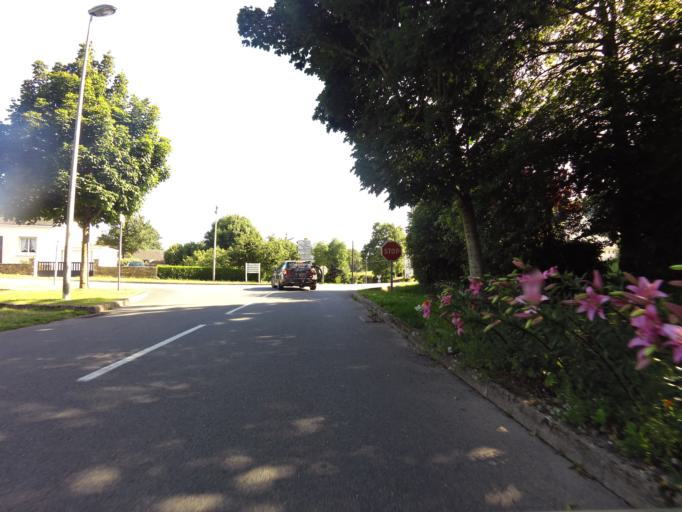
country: FR
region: Brittany
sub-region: Departement du Morbihan
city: Caden
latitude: 47.6308
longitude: -2.2895
